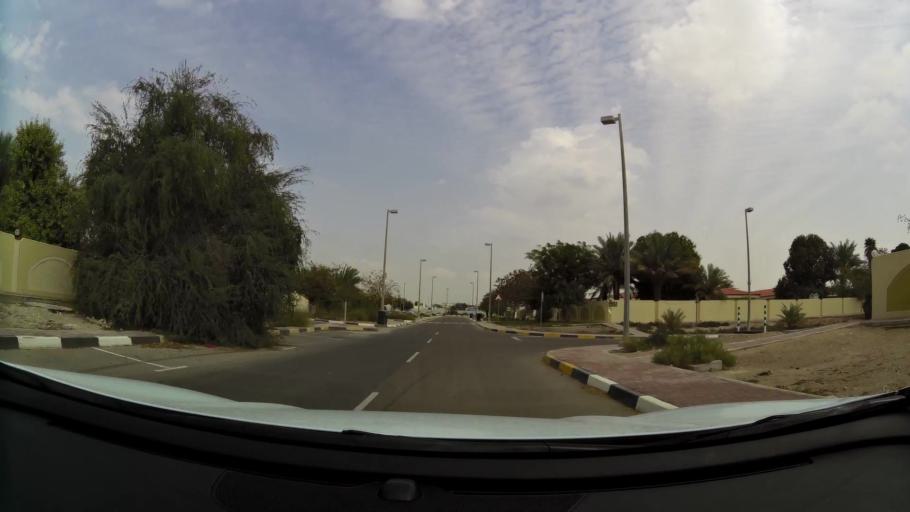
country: AE
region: Abu Dhabi
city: Abu Dhabi
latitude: 24.5218
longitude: 54.6820
